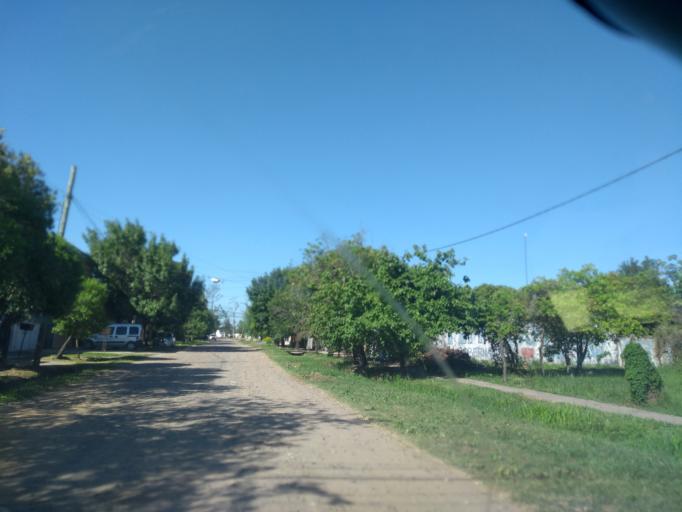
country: AR
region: Chaco
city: Resistencia
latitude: -27.4728
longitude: -58.9798
